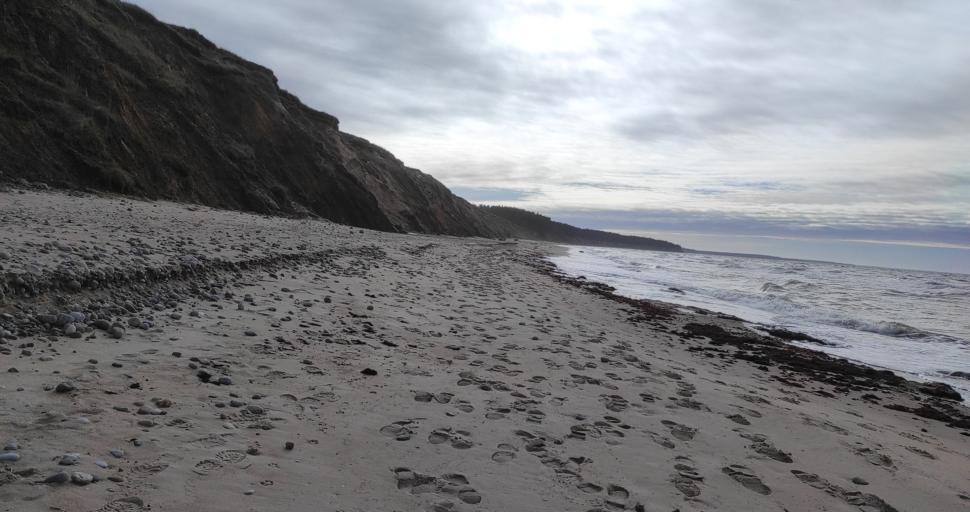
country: LV
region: Alsunga
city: Alsunga
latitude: 57.0393
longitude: 21.4026
